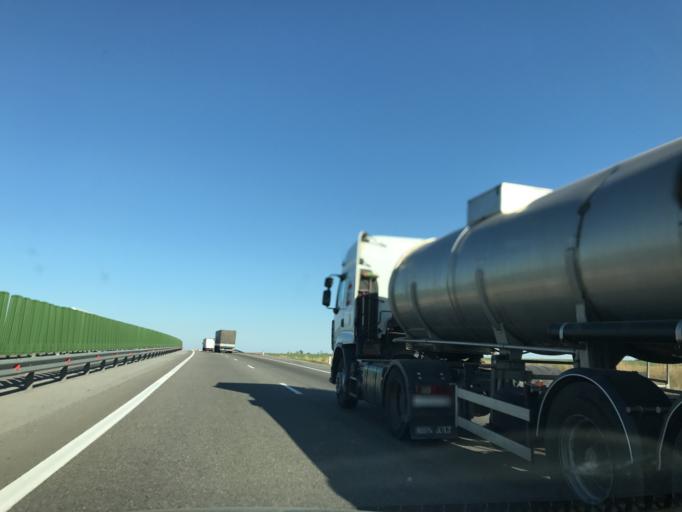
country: RU
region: Rostov
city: Tarasovskiy
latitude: 48.7382
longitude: 40.3995
